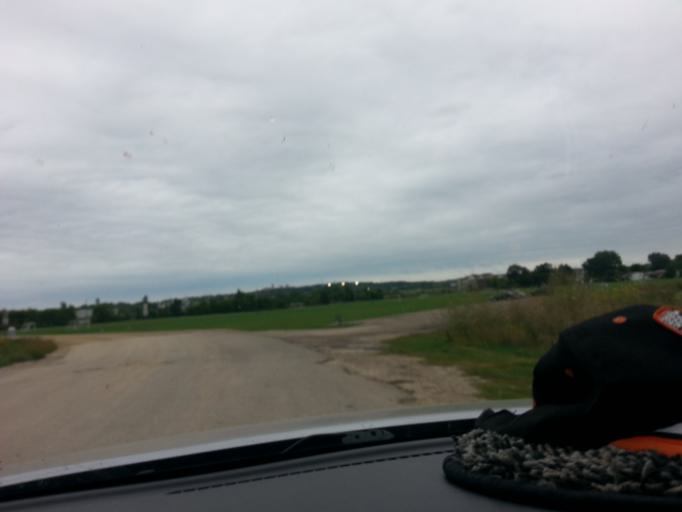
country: US
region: Minnesota
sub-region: Olmsted County
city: Rochester
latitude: 44.0234
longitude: -92.4988
